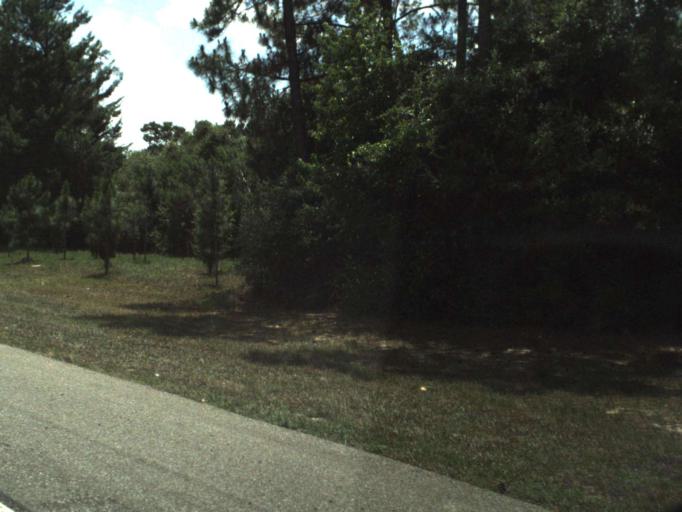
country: US
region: Florida
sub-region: Volusia County
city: Deltona
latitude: 28.9295
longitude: -81.2661
